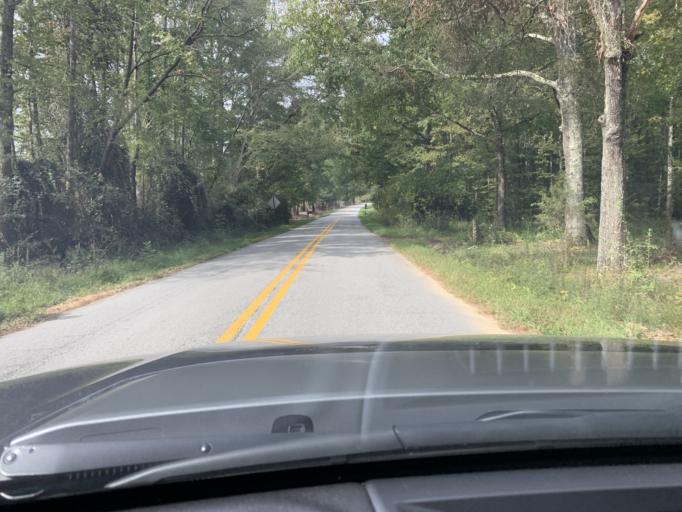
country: US
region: Georgia
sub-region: Polk County
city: Cedartown
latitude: 33.9744
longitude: -85.2898
